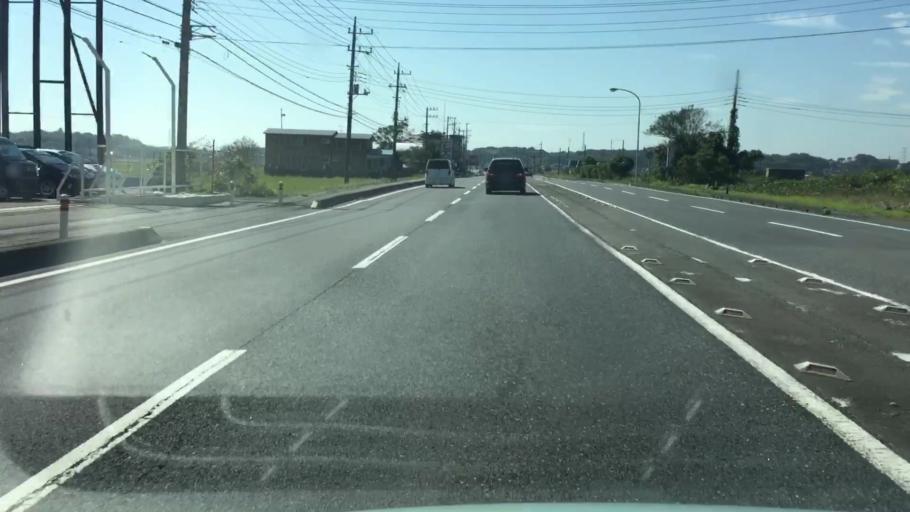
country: JP
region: Ibaraki
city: Ryugasaki
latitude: 35.8939
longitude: 140.1634
